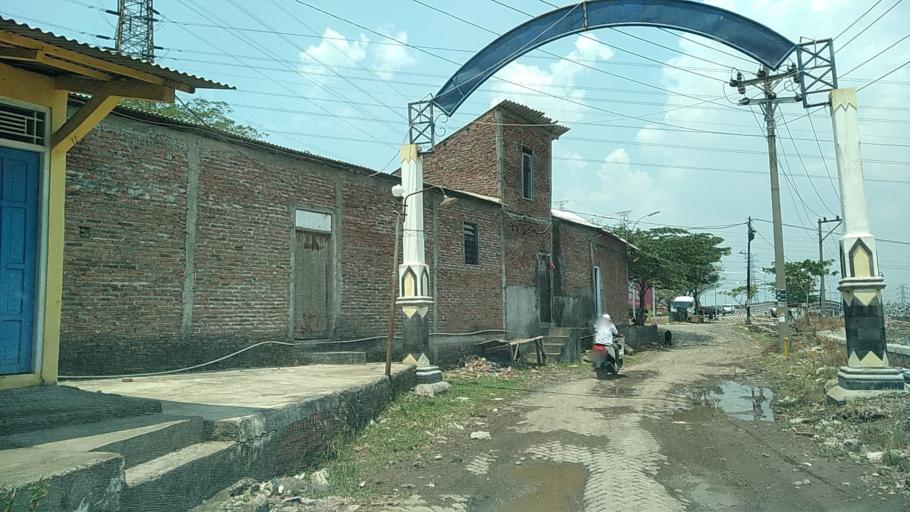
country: ID
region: Central Java
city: Semarang
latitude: -6.9519
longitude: 110.4376
